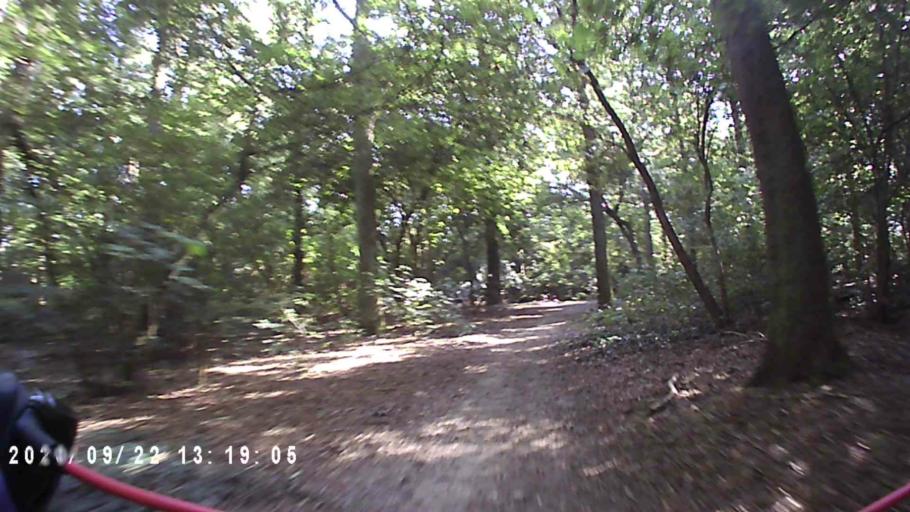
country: NL
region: Groningen
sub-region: Gemeente Leek
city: Leek
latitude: 53.1729
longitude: 6.3778
